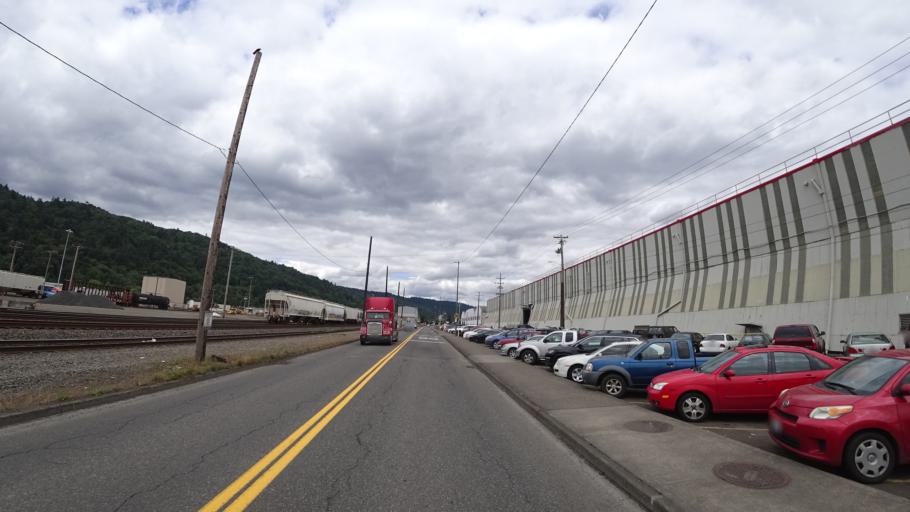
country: US
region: Oregon
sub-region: Multnomah County
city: Portland
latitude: 45.5553
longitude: -122.7241
